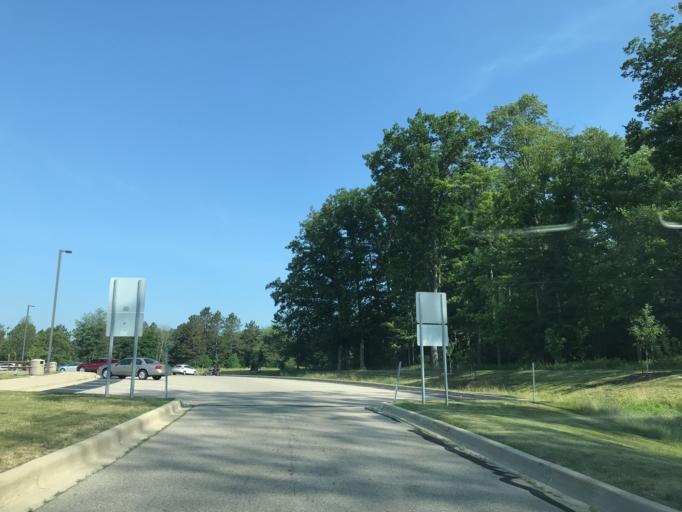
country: US
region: Michigan
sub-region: Ingham County
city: Okemos
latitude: 42.6775
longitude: -84.4048
